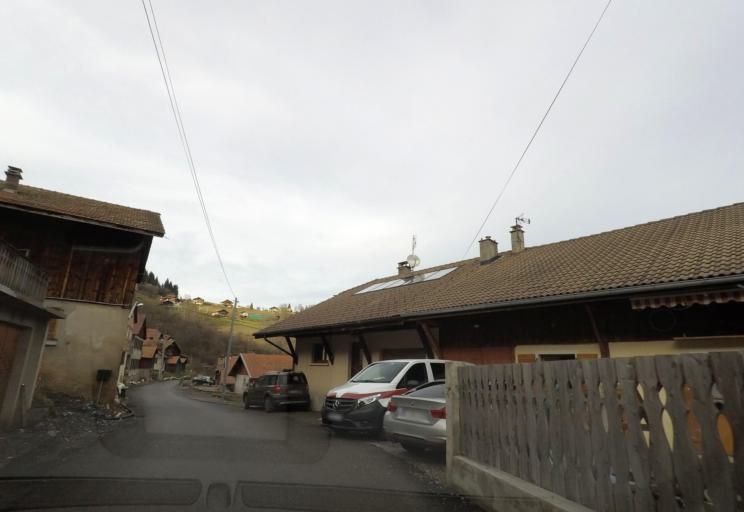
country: FR
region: Rhone-Alpes
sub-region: Departement de la Haute-Savoie
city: Ayse
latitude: 46.0477
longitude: 6.4449
